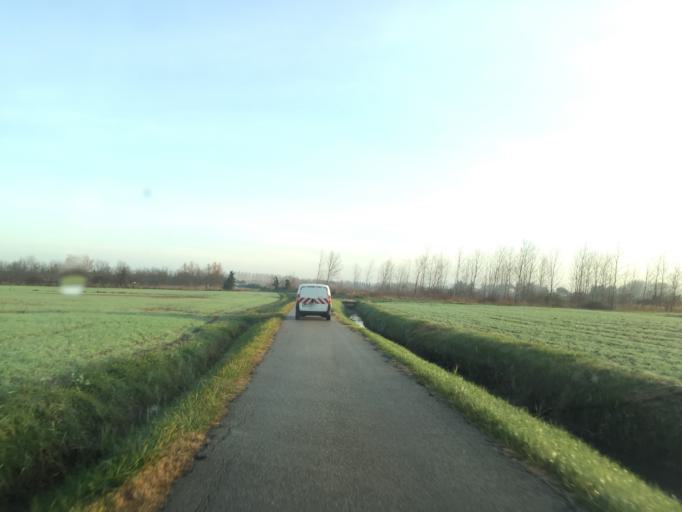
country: FR
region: Provence-Alpes-Cote d'Azur
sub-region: Departement du Vaucluse
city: Caderousse
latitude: 44.1135
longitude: 4.7599
